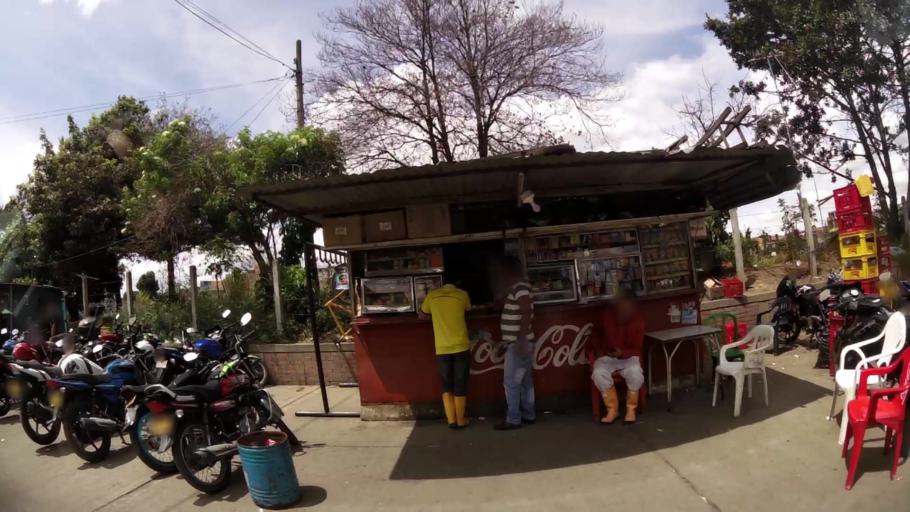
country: CO
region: Bogota D.C.
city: Bogota
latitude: 4.6526
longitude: -74.1334
